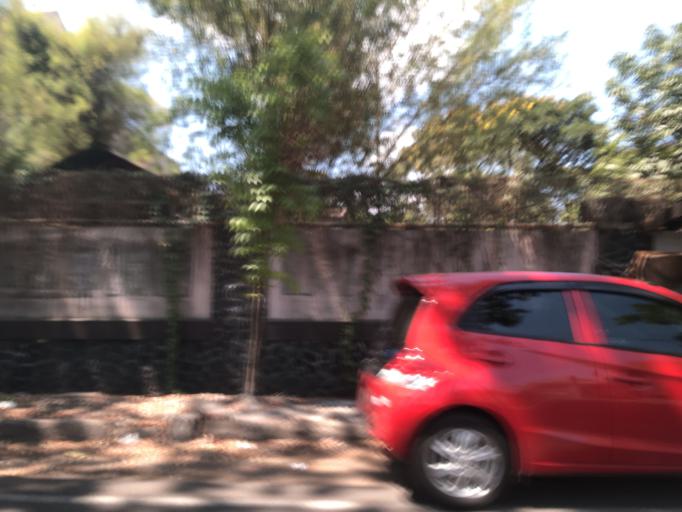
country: ID
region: West Java
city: Bandung
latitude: -6.9116
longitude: 107.6317
